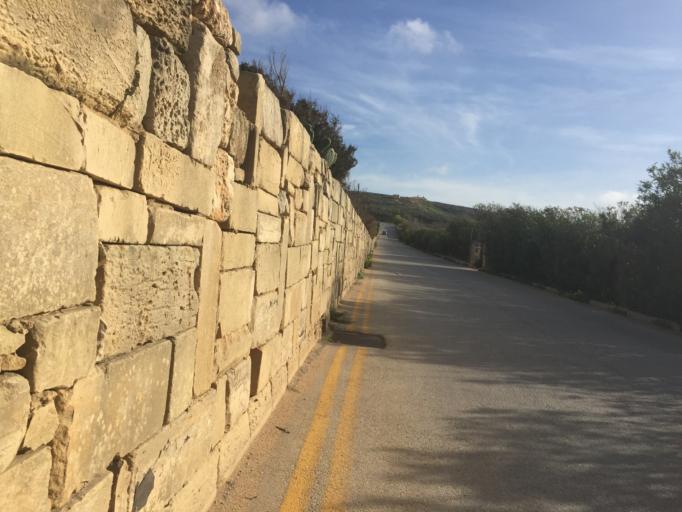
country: MT
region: L-Imgarr
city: Imgarr
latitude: 35.9332
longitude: 14.3465
